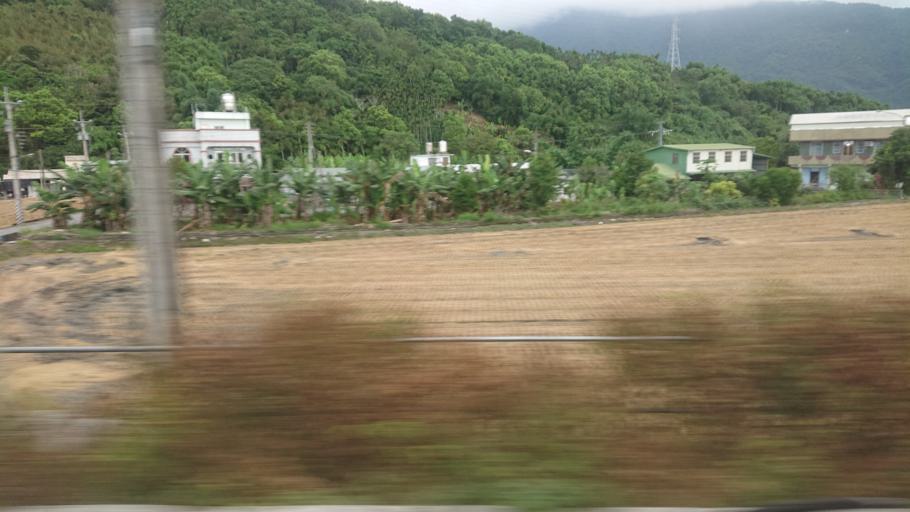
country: TW
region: Taiwan
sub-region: Hualien
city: Hualian
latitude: 23.7322
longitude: 121.4394
